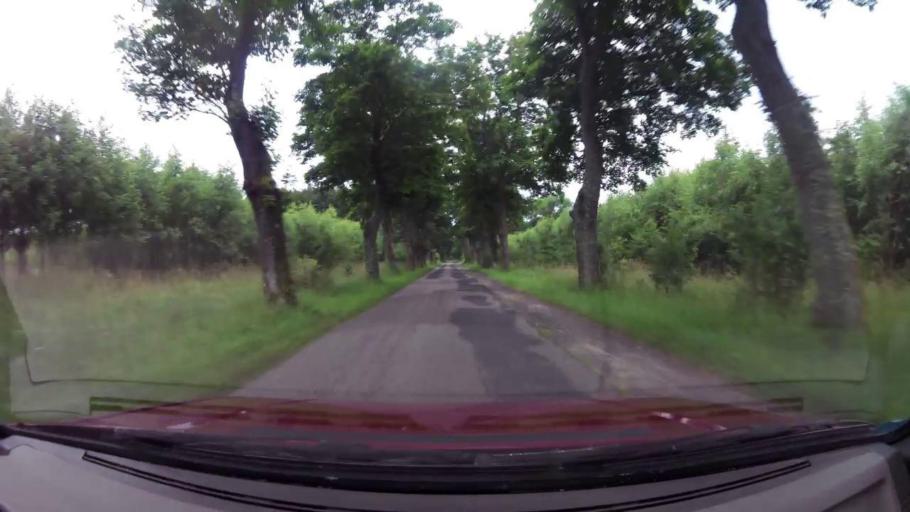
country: PL
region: West Pomeranian Voivodeship
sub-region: Powiat swidwinski
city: Rabino
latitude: 53.9261
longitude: 15.9632
